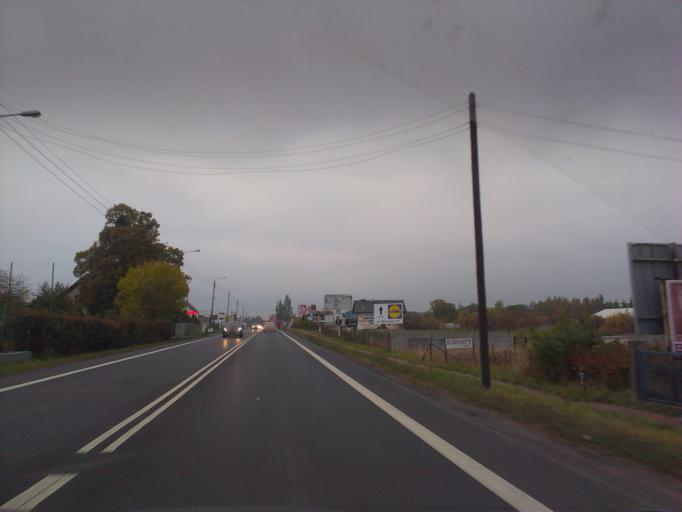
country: PL
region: Greater Poland Voivodeship
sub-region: Powiat poznanski
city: Suchy Las
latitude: 52.4706
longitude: 16.8809
